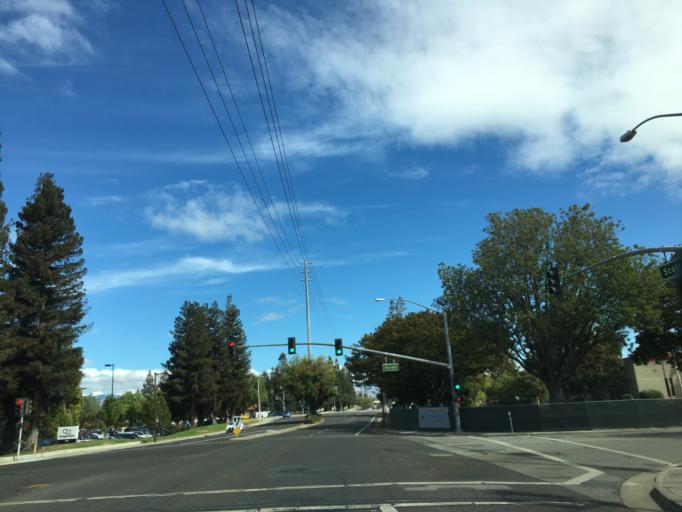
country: US
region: California
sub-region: Santa Clara County
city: Santa Clara
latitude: 37.3789
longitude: -121.9680
